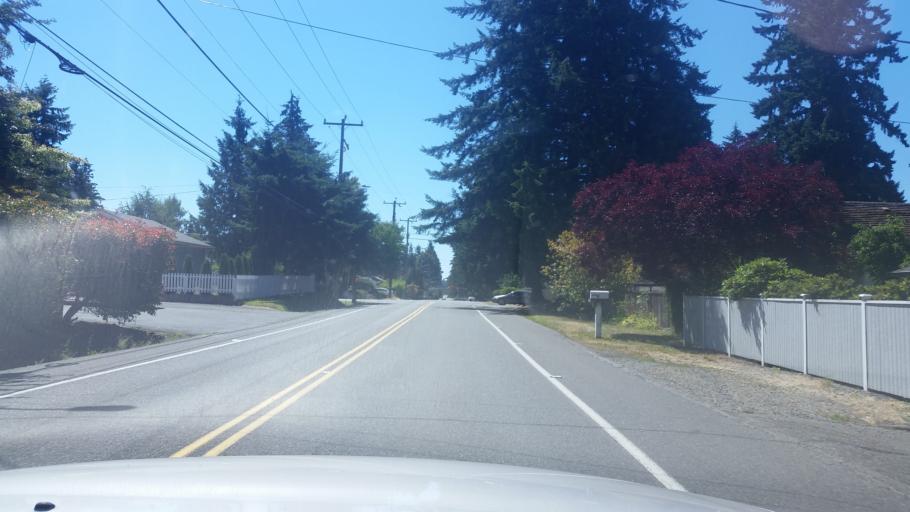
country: US
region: Washington
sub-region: King County
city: Shoreline
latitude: 47.7657
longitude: -122.3513
